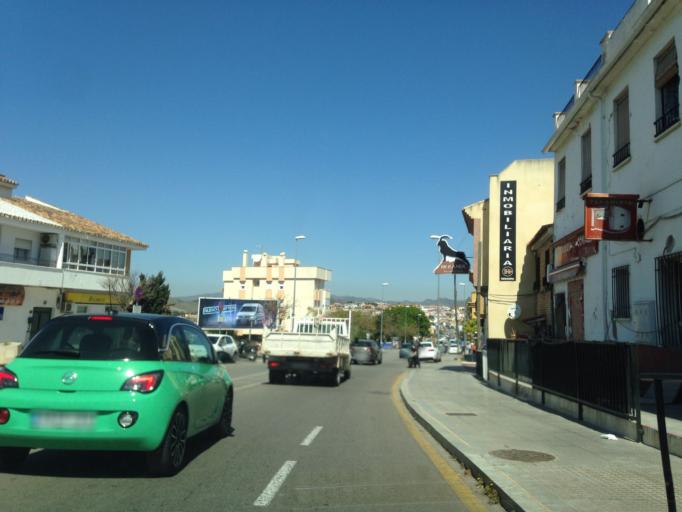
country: ES
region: Andalusia
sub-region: Provincia de Malaga
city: Malaga
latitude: 36.7337
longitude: -4.4775
